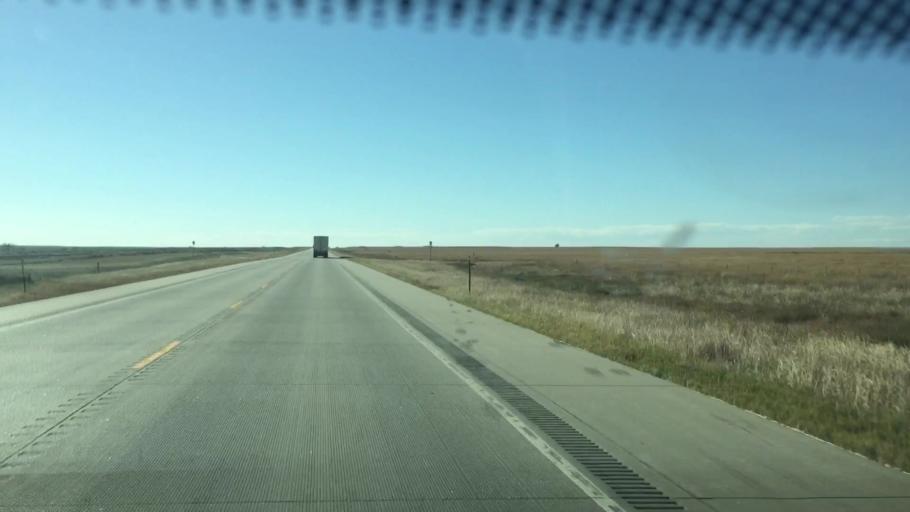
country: US
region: Colorado
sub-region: Kiowa County
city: Eads
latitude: 38.7647
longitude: -102.8334
